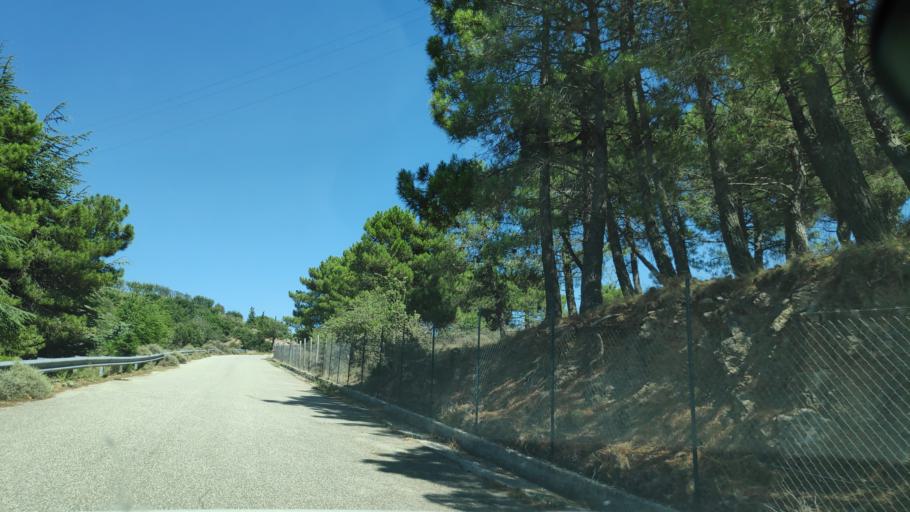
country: IT
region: Calabria
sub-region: Provincia di Reggio Calabria
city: Bova
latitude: 38.0253
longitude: 15.9414
